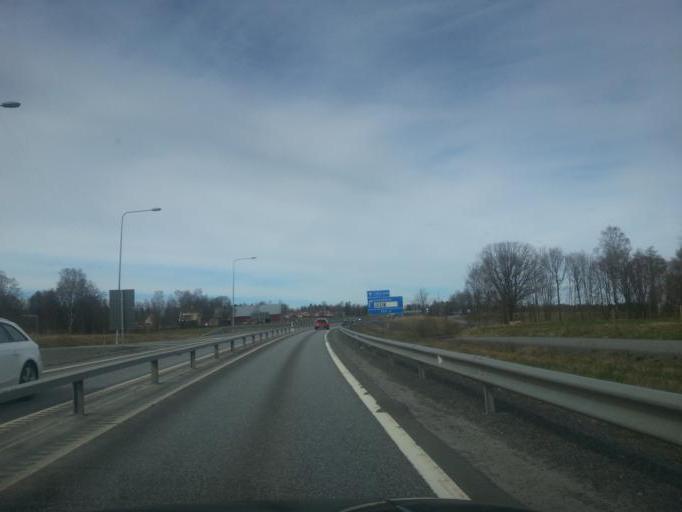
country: SE
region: Joenkoeping
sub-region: Jonkopings Kommun
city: Bankeryd
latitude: 57.8853
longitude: 14.1029
